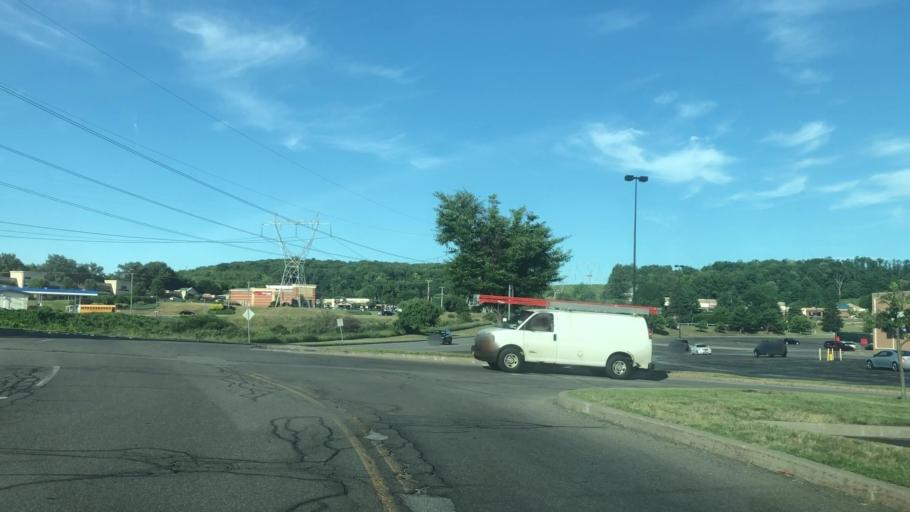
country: US
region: New York
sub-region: Ontario County
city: Victor
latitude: 43.0316
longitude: -77.4454
